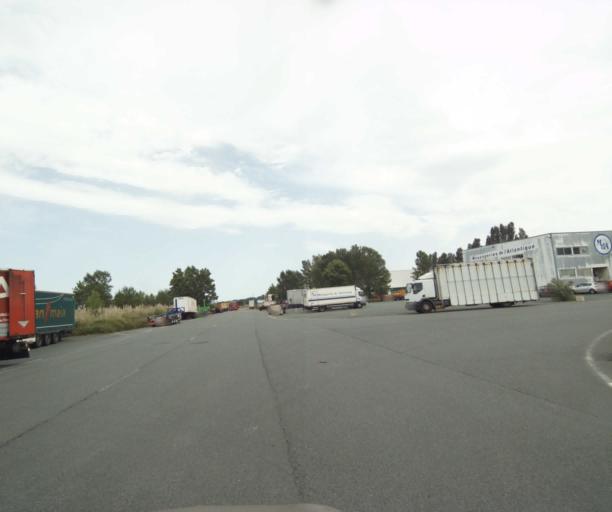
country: FR
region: Aquitaine
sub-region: Departement des Pyrenees-Atlantiques
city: Mouguerre
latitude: 43.4850
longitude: -1.4264
